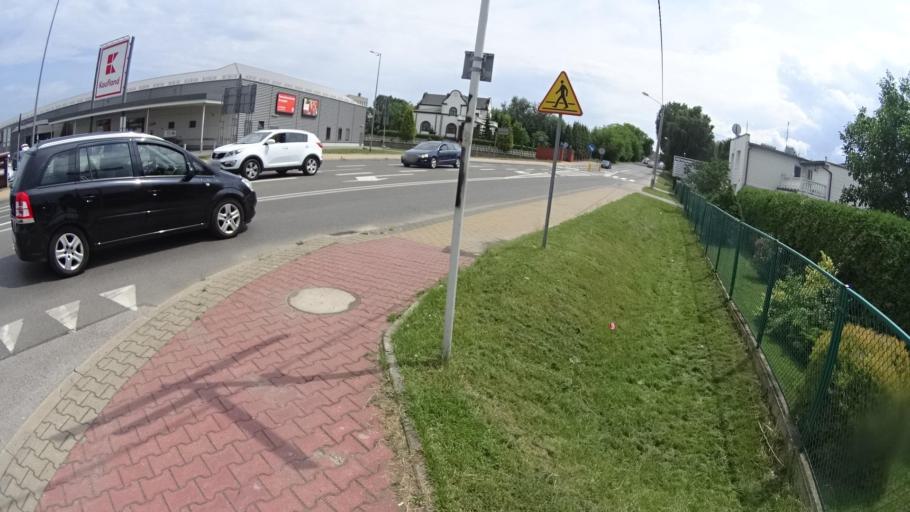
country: PL
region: Masovian Voivodeship
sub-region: Powiat grojecki
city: Grojec
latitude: 51.8719
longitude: 20.8648
